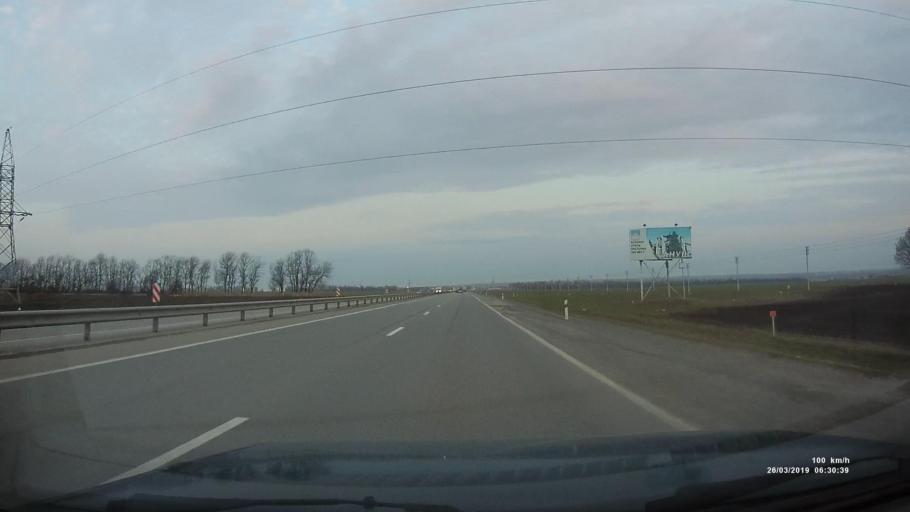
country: RU
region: Rostov
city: Krym
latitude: 47.2715
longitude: 39.5490
